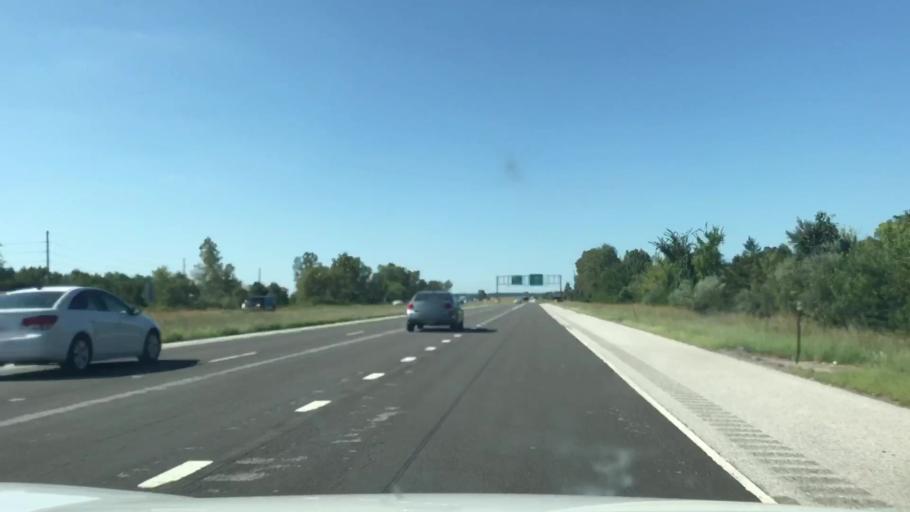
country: US
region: Illinois
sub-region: Madison County
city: South Roxana
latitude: 38.8443
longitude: -90.0466
